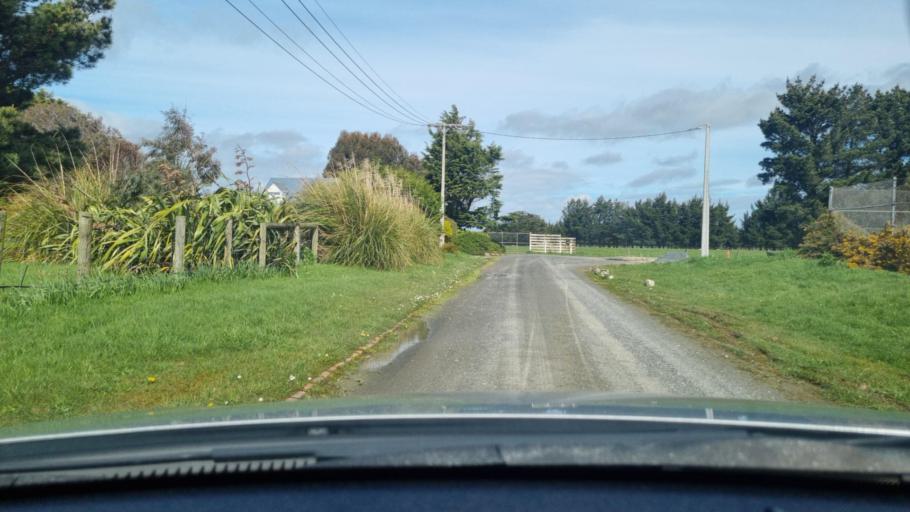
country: NZ
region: Southland
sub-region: Invercargill City
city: Invercargill
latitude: -46.4545
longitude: 168.3710
